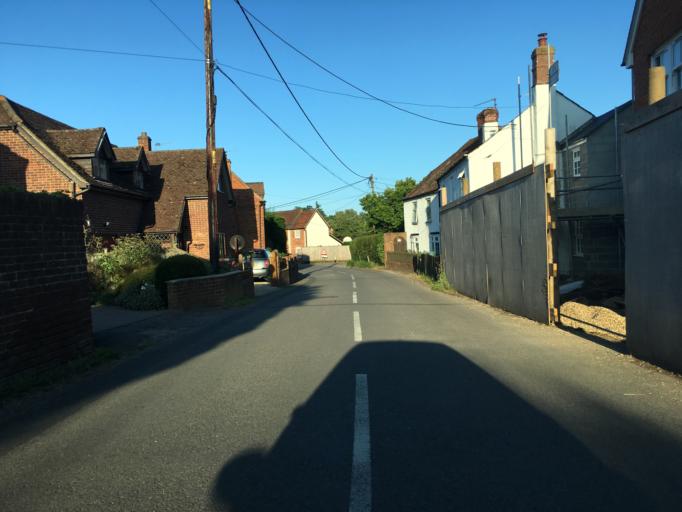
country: GB
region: England
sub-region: Hampshire
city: Tadley
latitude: 51.4160
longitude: -1.1604
